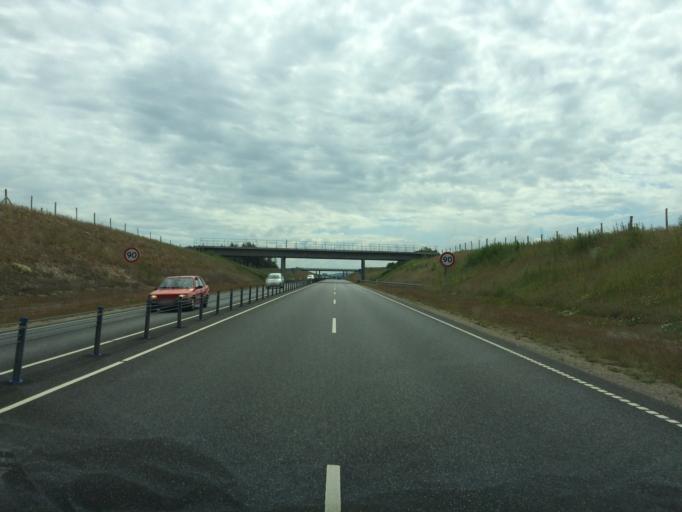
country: DK
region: Zealand
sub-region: Odsherred Kommune
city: Hojby
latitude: 55.8626
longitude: 11.5921
